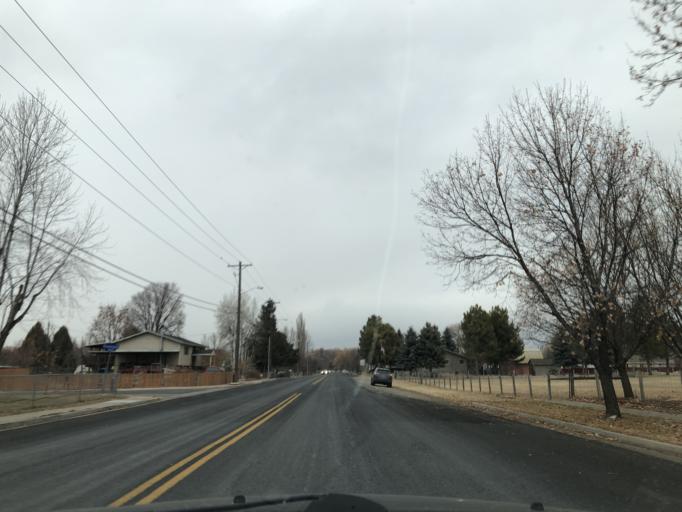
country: US
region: Utah
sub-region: Cache County
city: Logan
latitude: 41.7137
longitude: -111.8528
